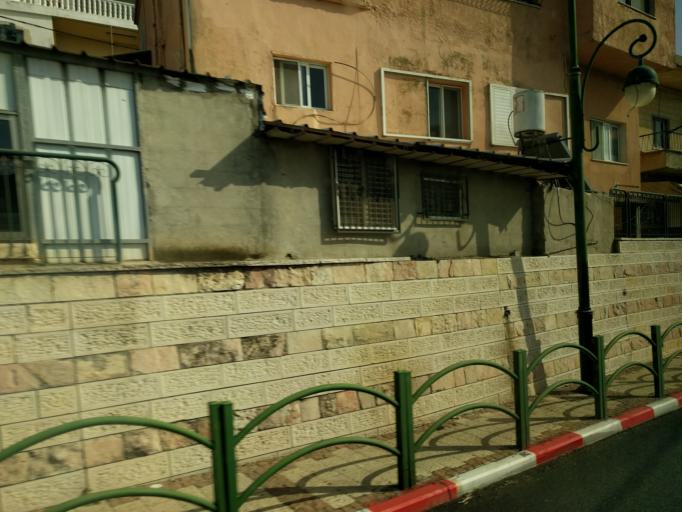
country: IL
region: Haifa
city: Daliyat el Karmil
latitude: 32.7180
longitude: 35.0653
